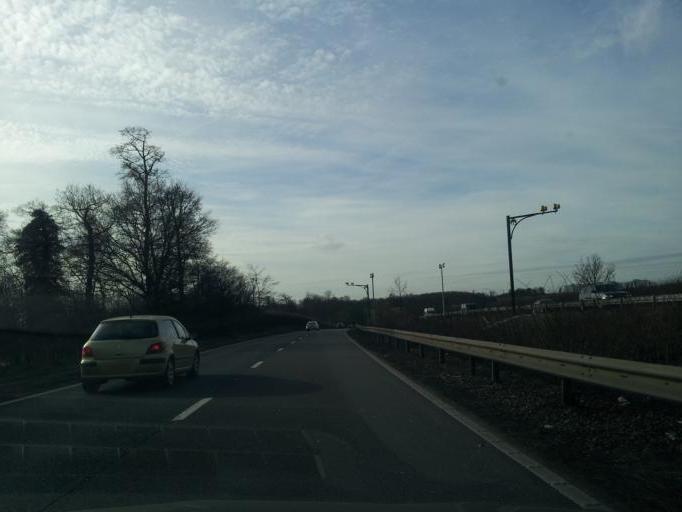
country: GB
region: England
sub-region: Cambridgeshire
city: Buckden
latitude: 52.2855
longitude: -0.2571
